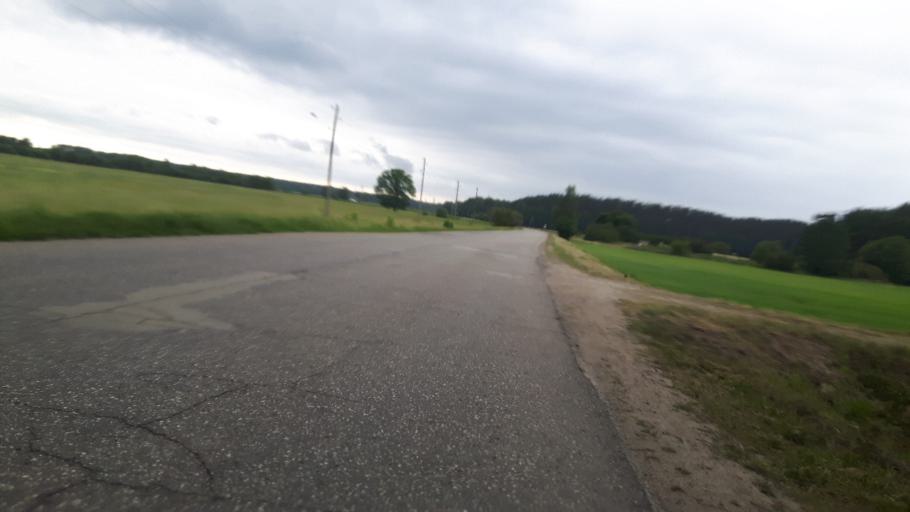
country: LV
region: Carnikava
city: Carnikava
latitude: 57.1167
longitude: 24.3128
